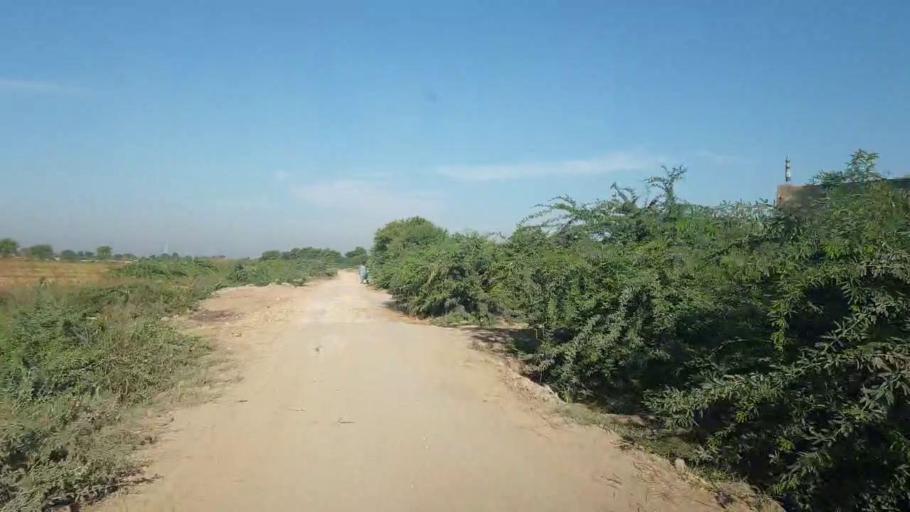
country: PK
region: Sindh
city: Talhar
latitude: 24.8259
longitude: 68.8209
